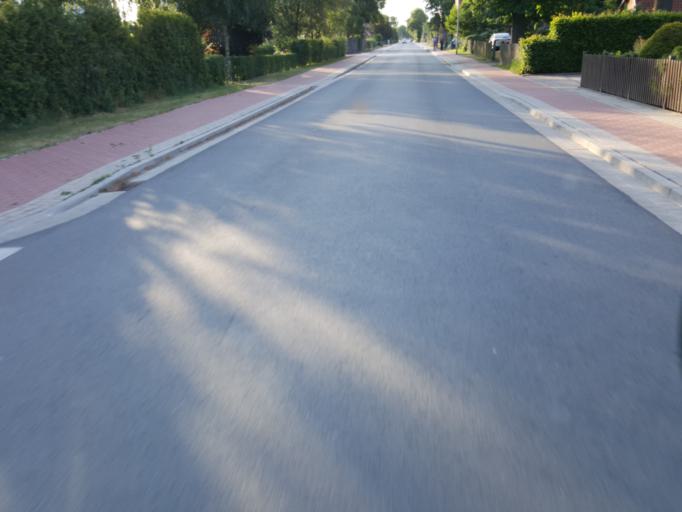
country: DE
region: Lower Saxony
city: Landesbergen
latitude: 52.5530
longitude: 9.1239
